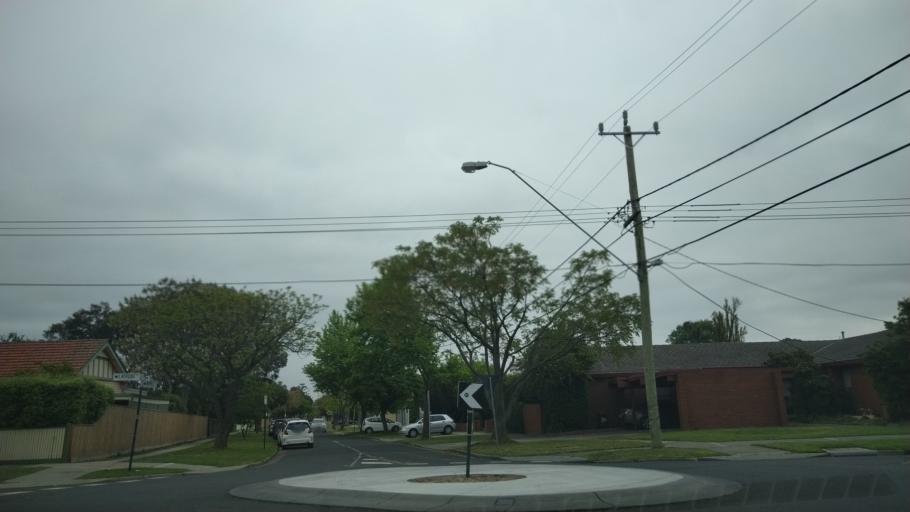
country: AU
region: Victoria
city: Hughesdale
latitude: -37.9033
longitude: 145.0842
